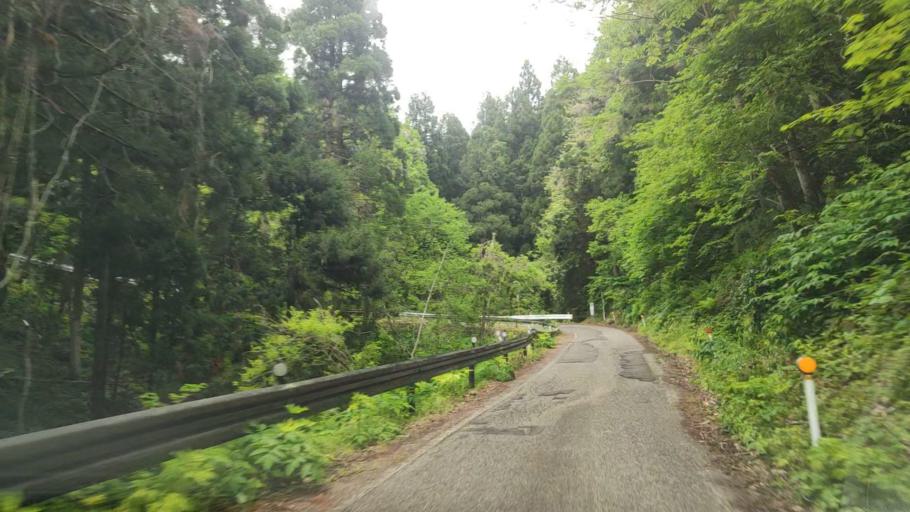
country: JP
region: Niigata
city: Kamo
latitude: 37.7149
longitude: 139.0910
